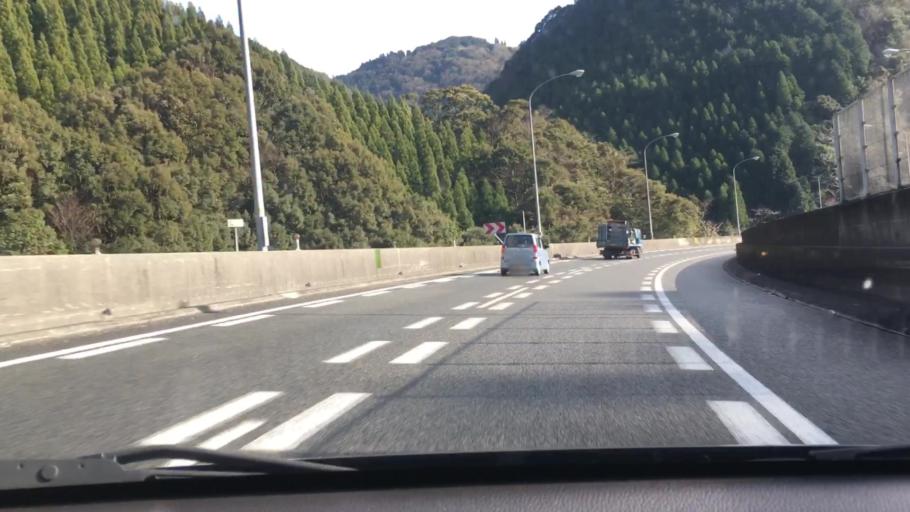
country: JP
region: Kumamoto
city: Hitoyoshi
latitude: 32.3259
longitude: 130.7575
